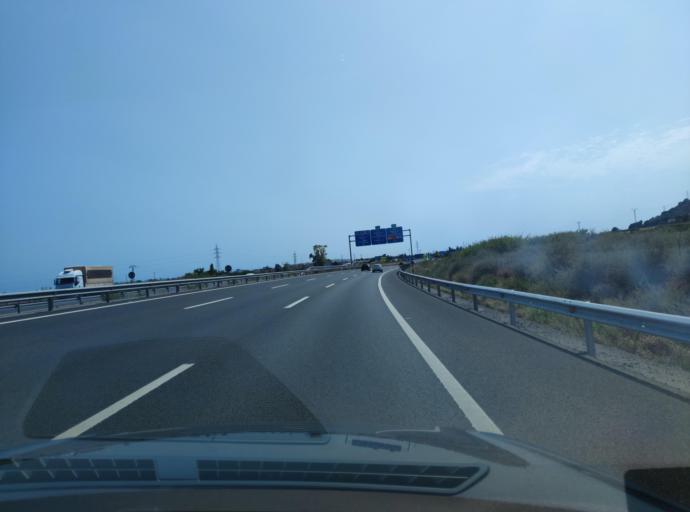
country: ES
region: Valencia
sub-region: Provincia de Valencia
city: Pucol
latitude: 39.6414
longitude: -0.3009
